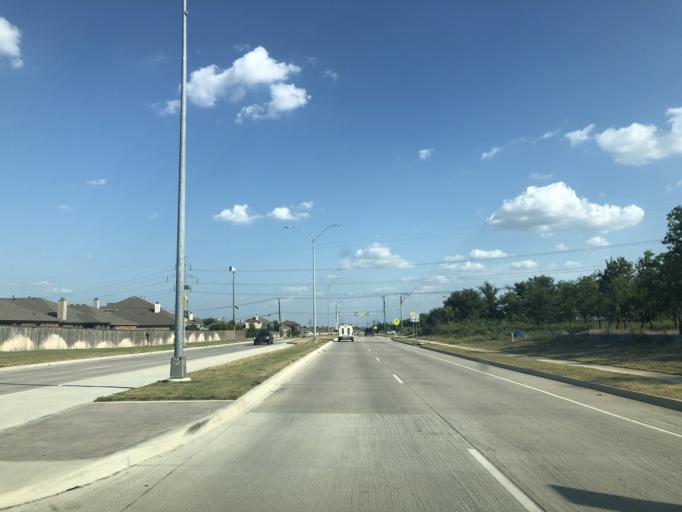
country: US
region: Texas
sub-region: Tarrant County
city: Saginaw
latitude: 32.8419
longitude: -97.3880
